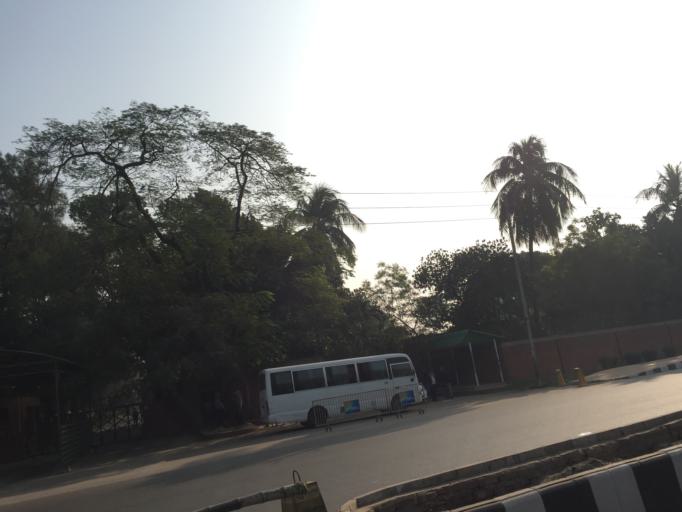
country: BD
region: Dhaka
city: Azimpur
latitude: 23.7651
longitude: 90.3704
